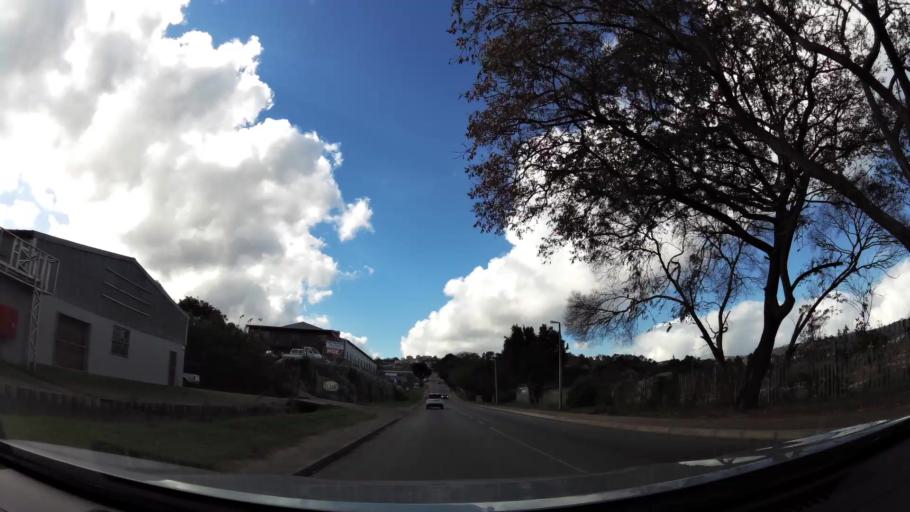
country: ZA
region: Western Cape
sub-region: Eden District Municipality
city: Knysna
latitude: -34.0471
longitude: 23.0733
